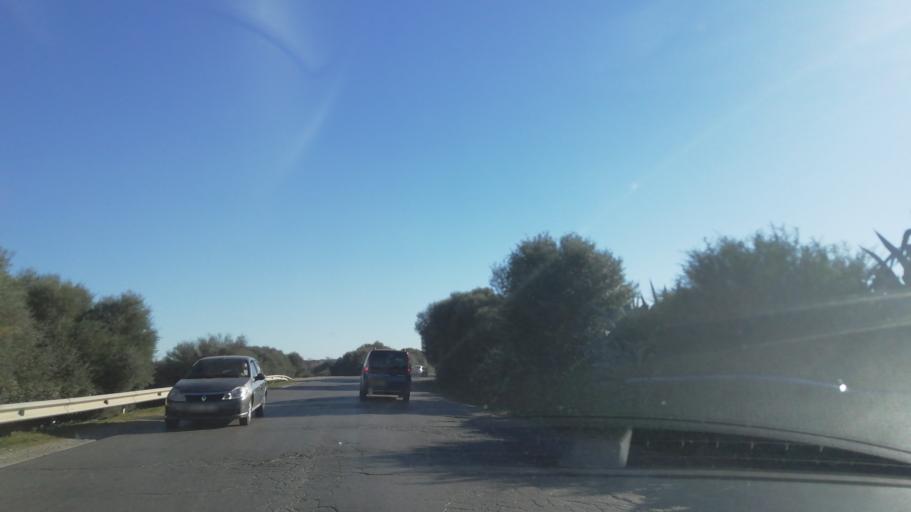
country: DZ
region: Relizane
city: Smala
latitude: 35.6954
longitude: 0.7822
